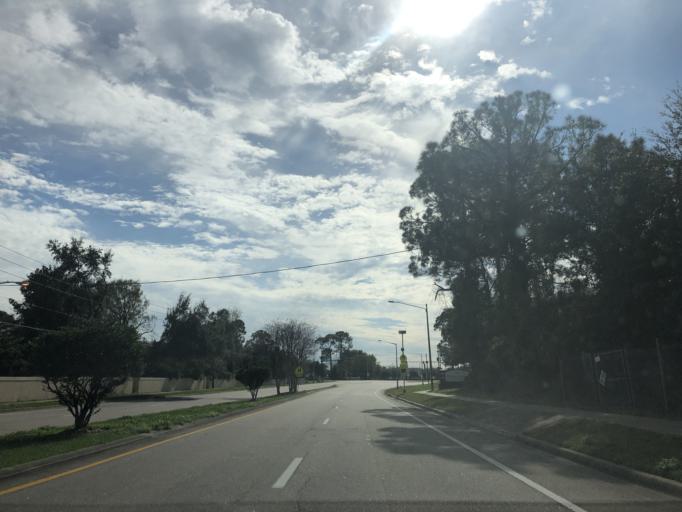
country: US
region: Florida
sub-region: Orange County
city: Bay Hill
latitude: 28.4866
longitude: -81.4918
